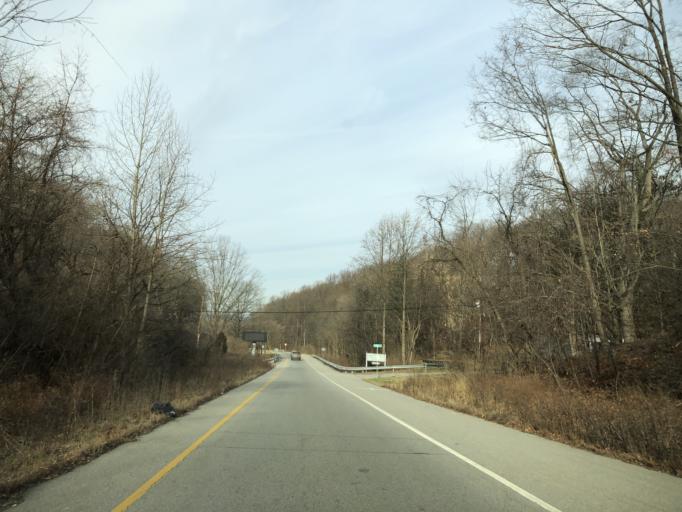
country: US
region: Pennsylvania
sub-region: Chester County
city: Exton
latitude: 40.0138
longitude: -75.6160
